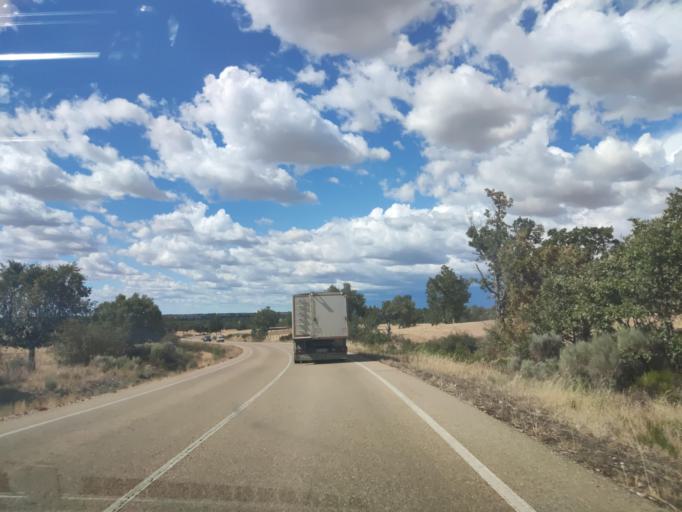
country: ES
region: Castille and Leon
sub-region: Provincia de Salamanca
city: Peralejos de Arriba
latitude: 40.9345
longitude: -6.3425
